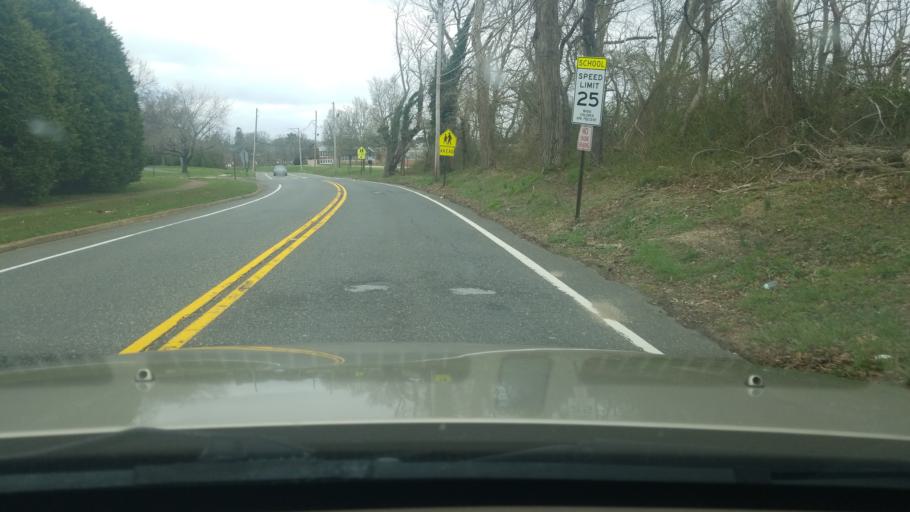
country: US
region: New Jersey
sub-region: Monmouth County
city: Ramtown
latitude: 40.1404
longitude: -74.1058
